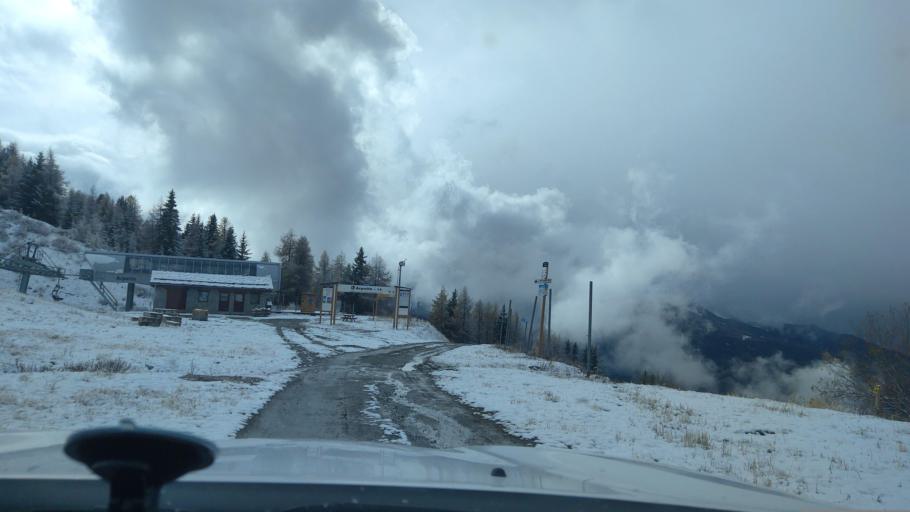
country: FR
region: Rhone-Alpes
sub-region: Departement de la Savoie
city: Seez
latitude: 45.5755
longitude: 6.7964
